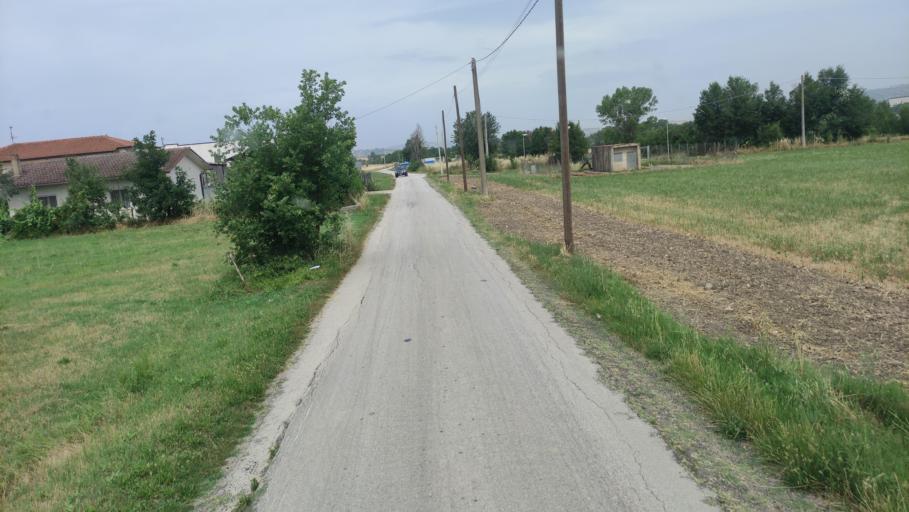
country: IT
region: Campania
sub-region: Provincia di Avellino
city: Sturno
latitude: 41.0511
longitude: 15.1240
